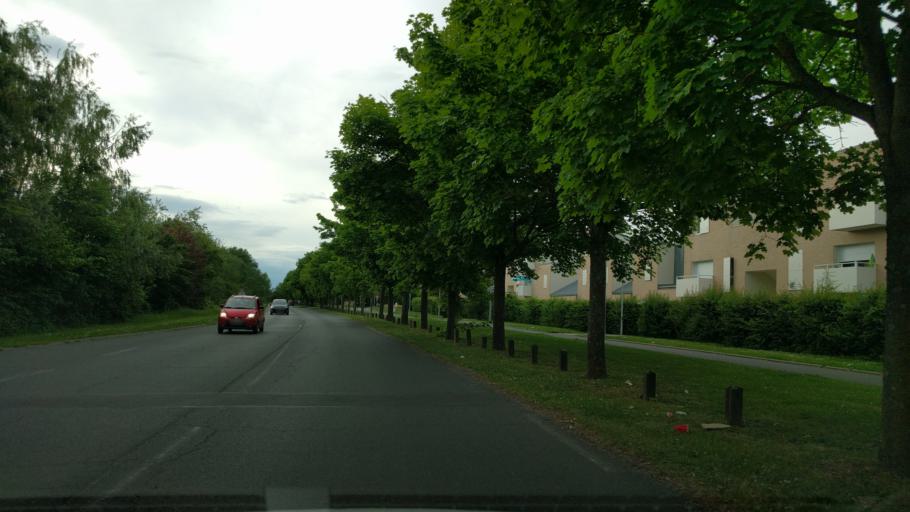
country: FR
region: Ile-de-France
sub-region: Departement de Seine-et-Marne
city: Savigny-le-Temple
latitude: 48.5680
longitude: 2.5921
